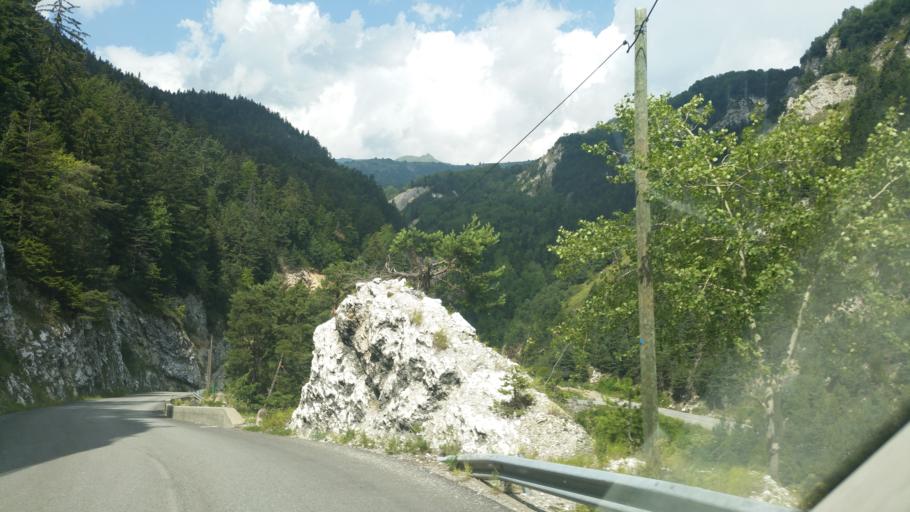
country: FR
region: Rhone-Alpes
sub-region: Departement de la Savoie
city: Saint-Jean-de-Maurienne
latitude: 45.2384
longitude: 6.3127
